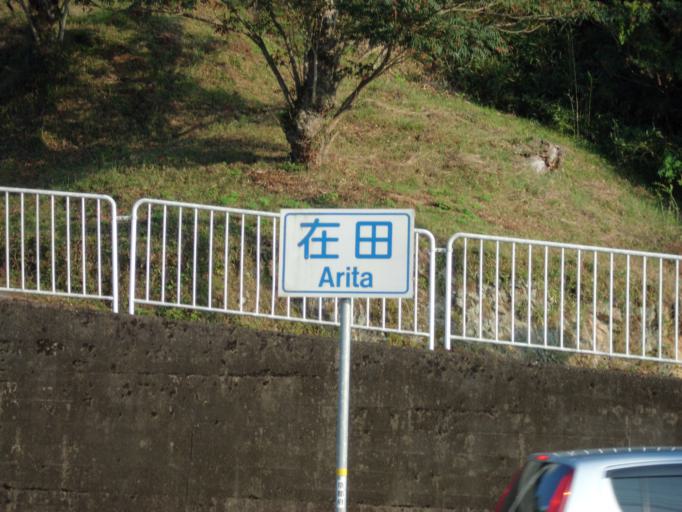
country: JP
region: Kyoto
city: Fukuchiyama
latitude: 35.3680
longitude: 135.1302
